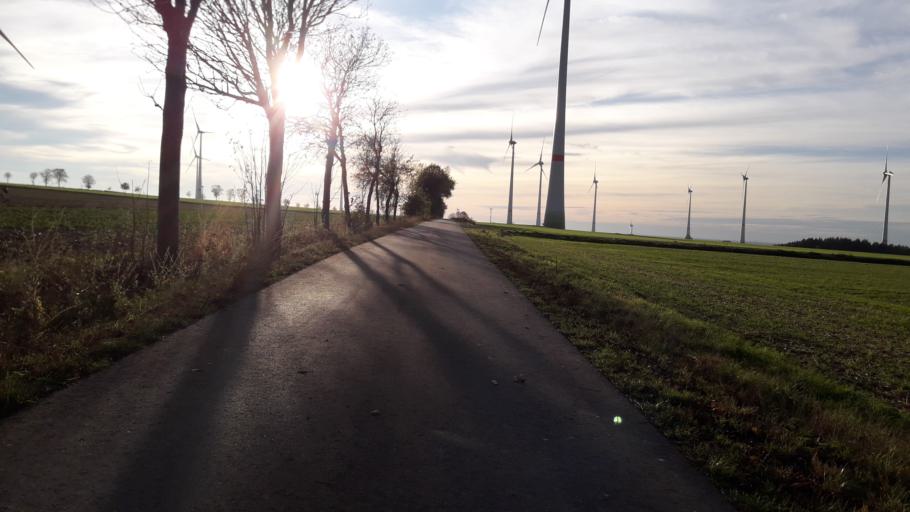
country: DE
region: North Rhine-Westphalia
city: Lichtenau
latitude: 51.6734
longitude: 8.8831
